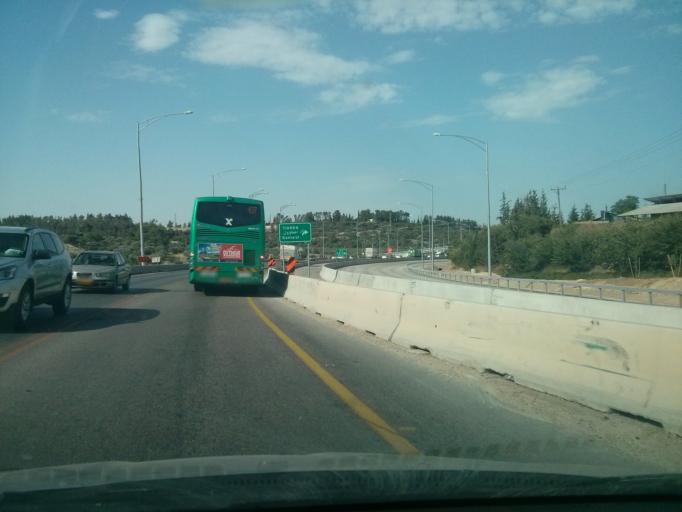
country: IL
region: Jerusalem
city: Bet Shemesh
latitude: 31.7802
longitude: 35.0142
